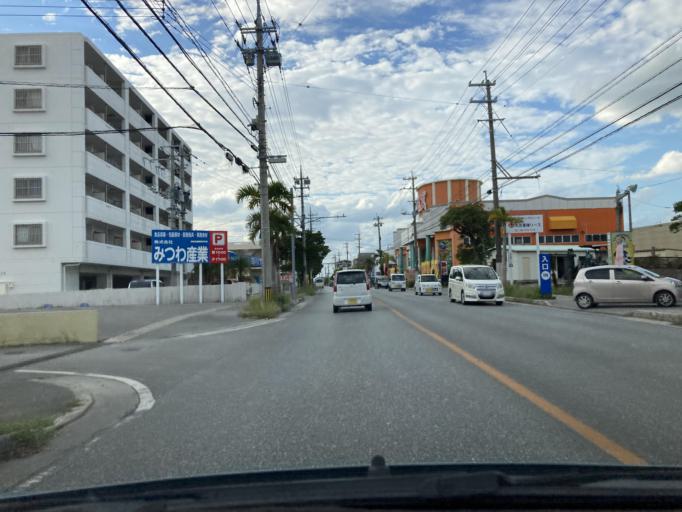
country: JP
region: Okinawa
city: Okinawa
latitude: 26.3593
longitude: 127.8228
